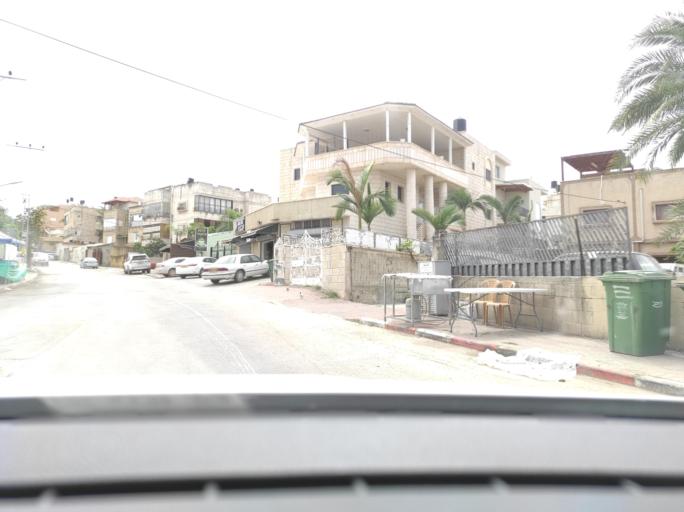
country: IL
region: Central District
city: Kafr Qasim
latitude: 32.1163
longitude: 34.9713
